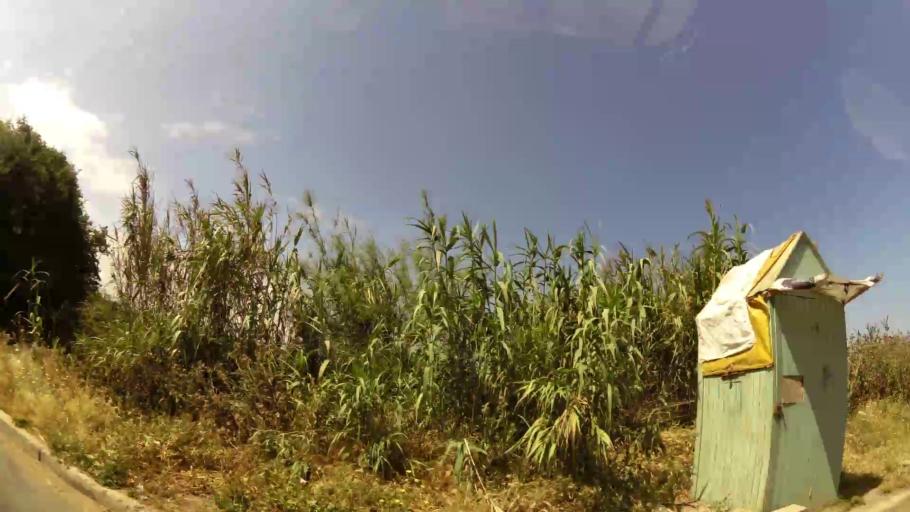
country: MA
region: Rabat-Sale-Zemmour-Zaer
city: Sale
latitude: 34.0760
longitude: -6.7742
